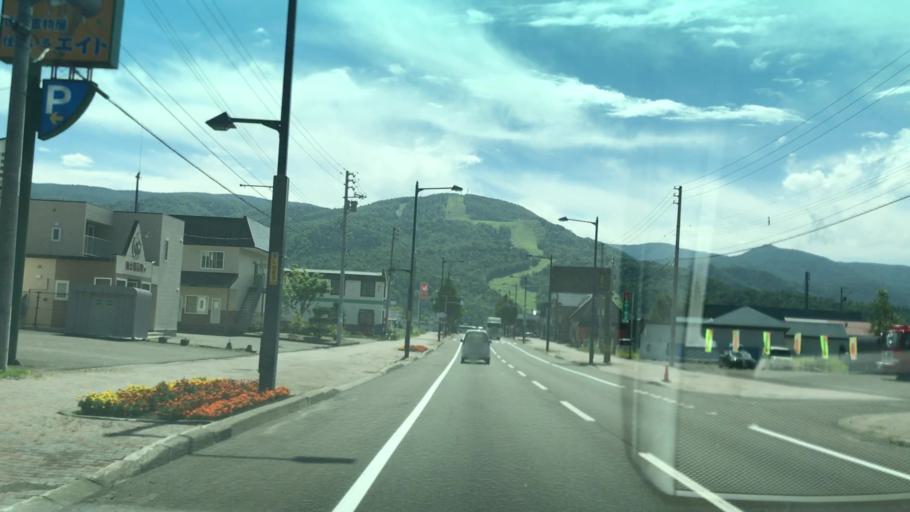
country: JP
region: Hokkaido
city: Shimo-furano
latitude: 42.8787
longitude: 142.4390
